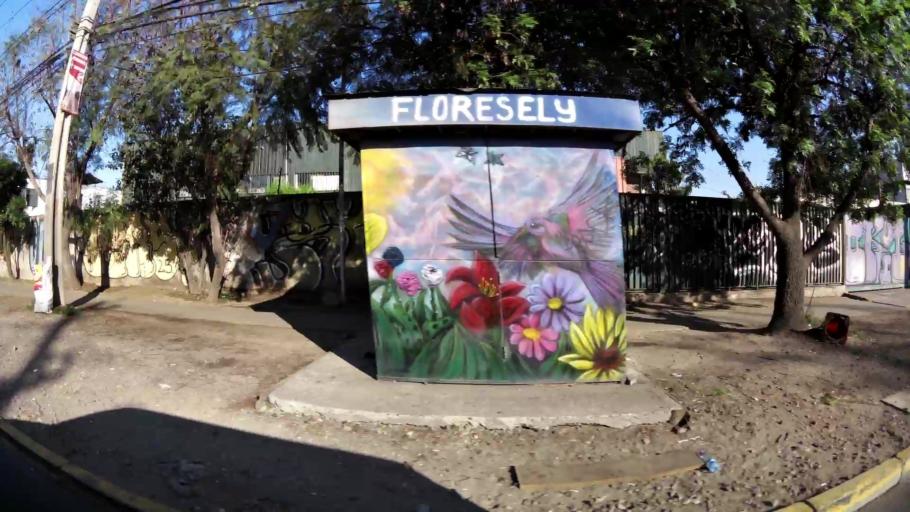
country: CL
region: Santiago Metropolitan
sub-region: Provincia de Santiago
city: Santiago
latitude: -33.3814
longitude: -70.6399
